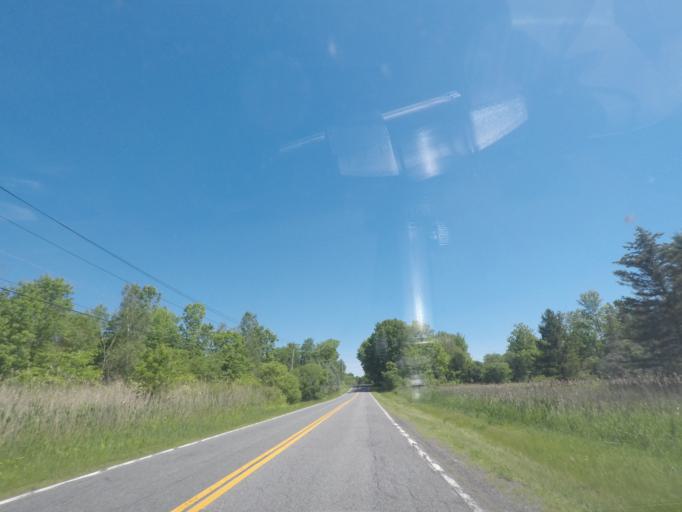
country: US
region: New York
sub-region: Schenectady County
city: East Glenville
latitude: 42.8876
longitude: -73.8638
